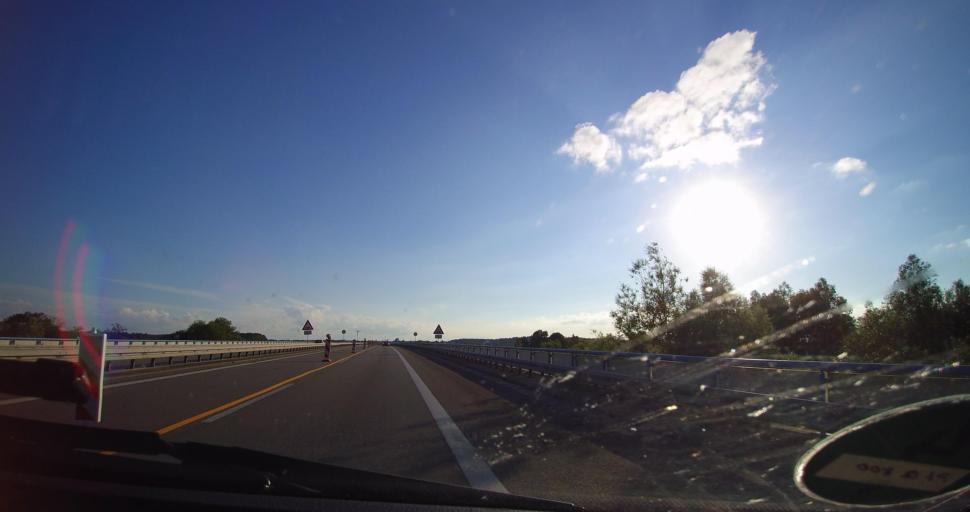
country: DE
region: Mecklenburg-Vorpommern
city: Tribsees
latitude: 54.0788
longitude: 12.7459
